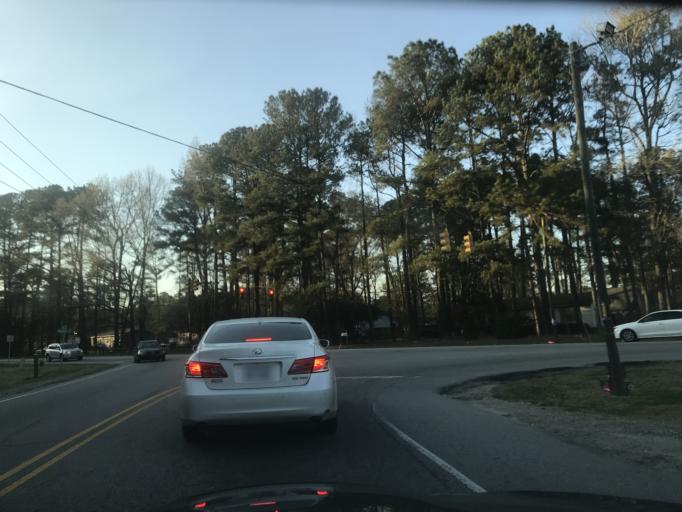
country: US
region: North Carolina
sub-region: Wake County
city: Knightdale
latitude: 35.7546
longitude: -78.5366
